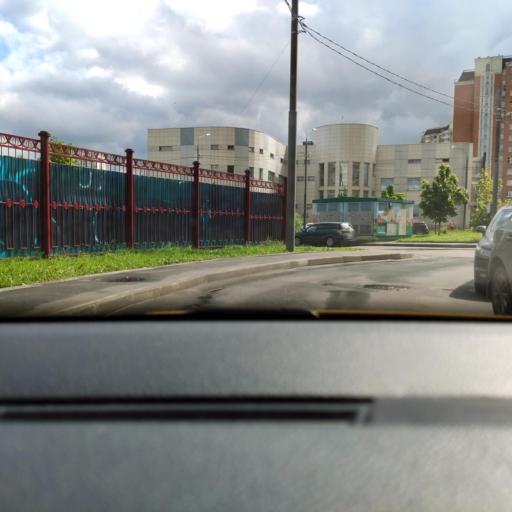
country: RU
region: Moscow
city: Nekrasovka
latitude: 55.7178
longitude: 37.8883
